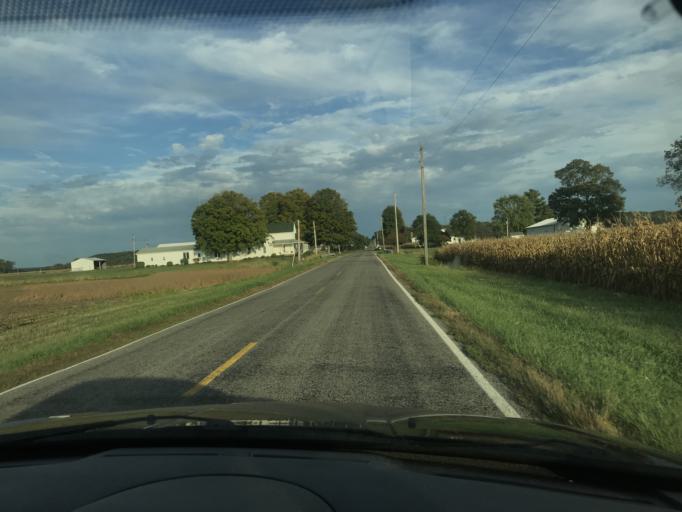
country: US
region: Ohio
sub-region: Logan County
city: West Liberty
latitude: 40.1942
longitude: -83.7889
